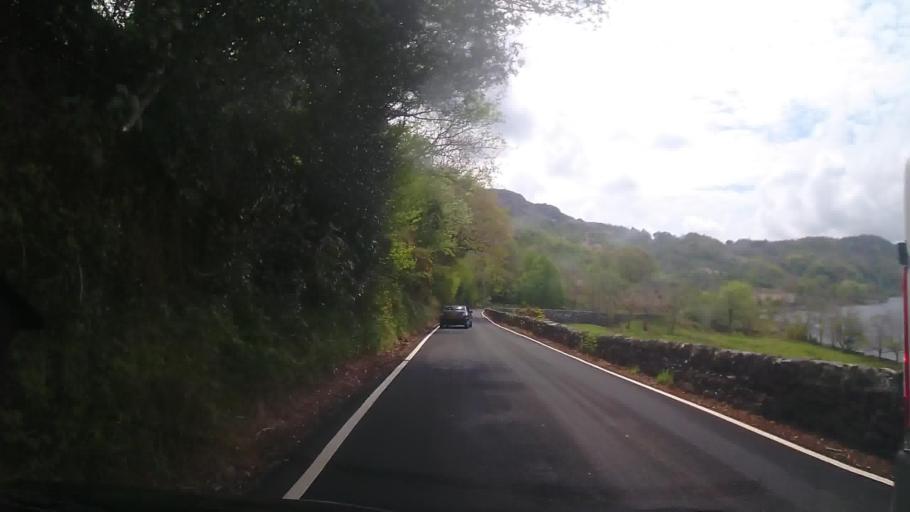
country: GB
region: Wales
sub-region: Gwynedd
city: Blaenau-Ffestiniog
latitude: 53.0503
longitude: -4.0140
